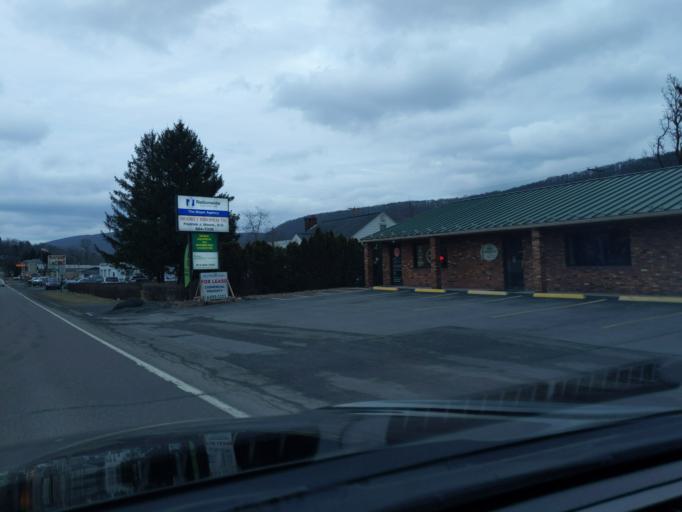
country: US
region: Pennsylvania
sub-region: Blair County
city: Tyrone
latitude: 40.6603
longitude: -78.2580
